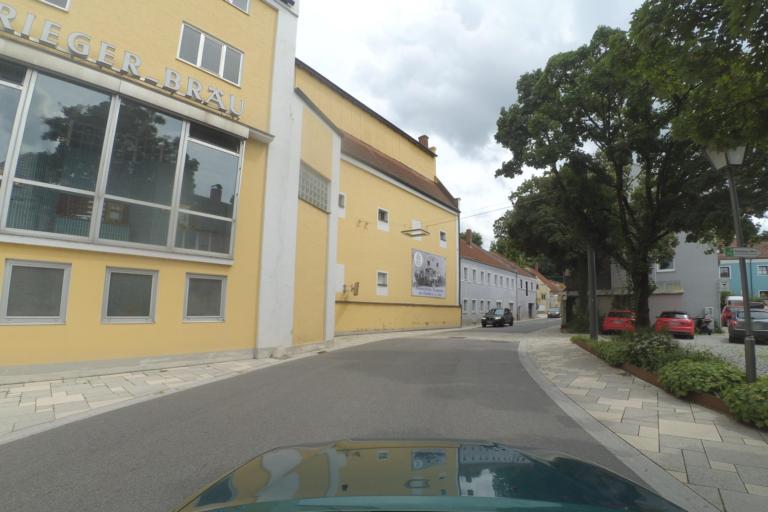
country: DE
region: Bavaria
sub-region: Lower Bavaria
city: Landau an der Isar
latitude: 48.6738
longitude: 12.6941
